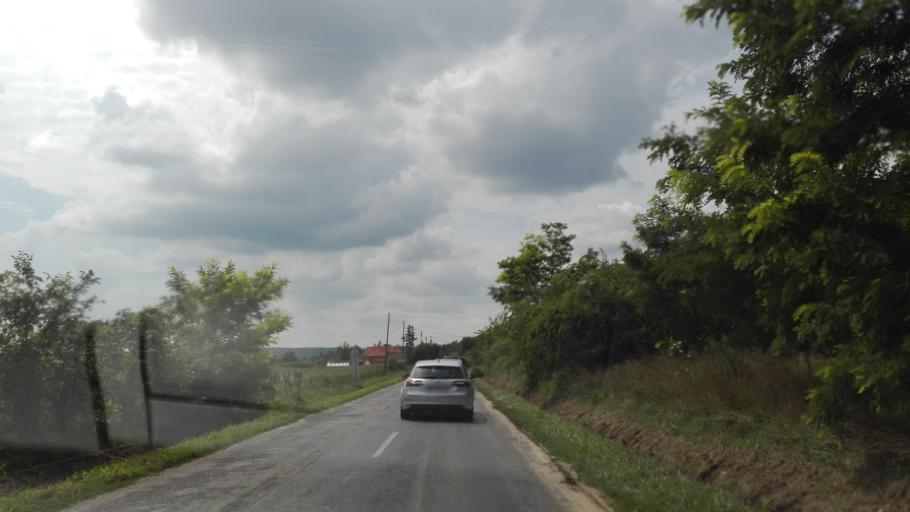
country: HU
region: Fejer
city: Mezoszilas
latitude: 46.7517
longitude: 18.4749
